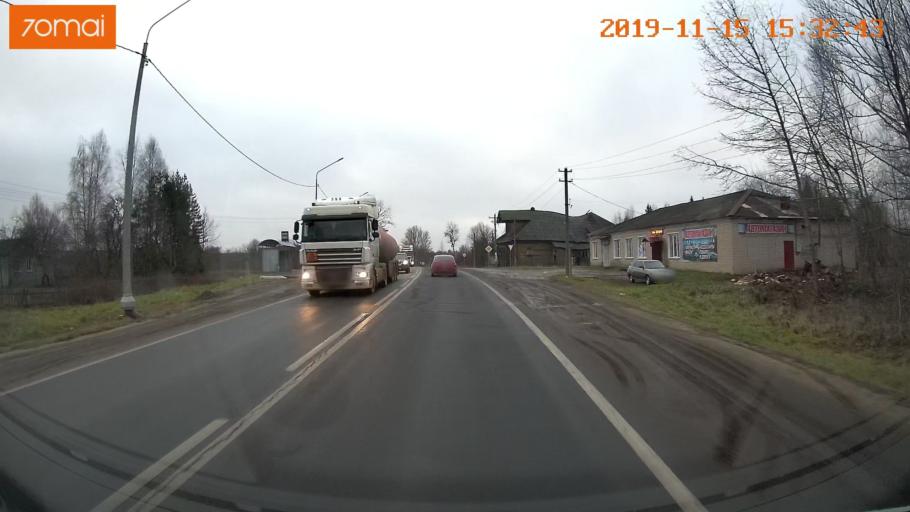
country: RU
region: Jaroslavl
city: Danilov
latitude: 58.0876
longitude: 40.0970
